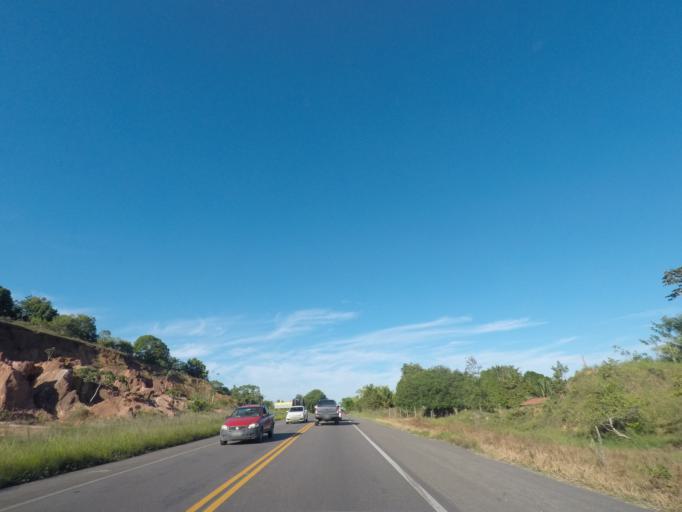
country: BR
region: Bahia
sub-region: Nazare
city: Nazare
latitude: -13.0123
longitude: -38.9740
